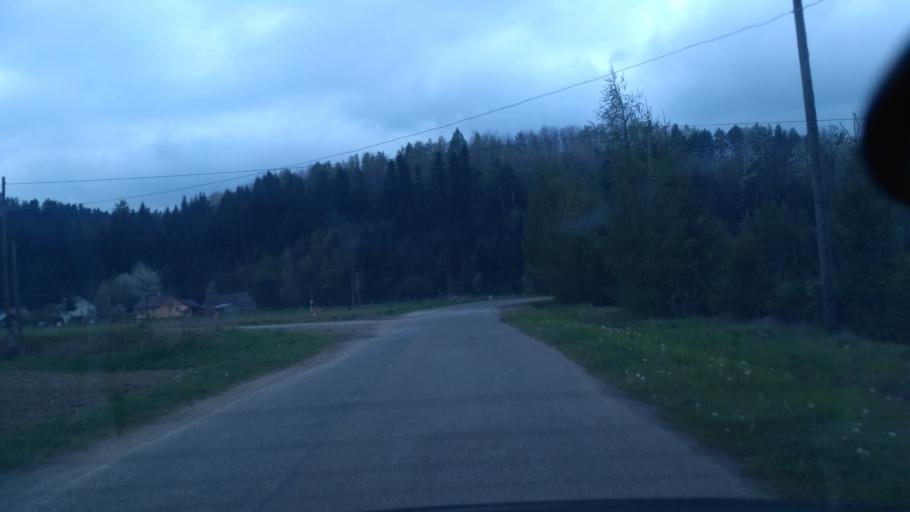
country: PL
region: Subcarpathian Voivodeship
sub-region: Powiat brzozowski
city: Dydnia
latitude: 49.6982
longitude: 22.1973
